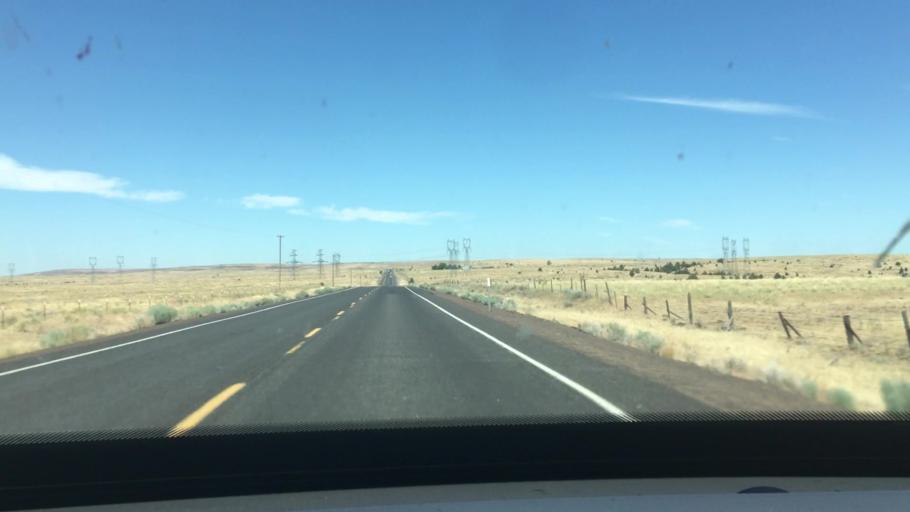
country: US
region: Oregon
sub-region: Jefferson County
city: Madras
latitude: 44.9482
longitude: -120.9105
